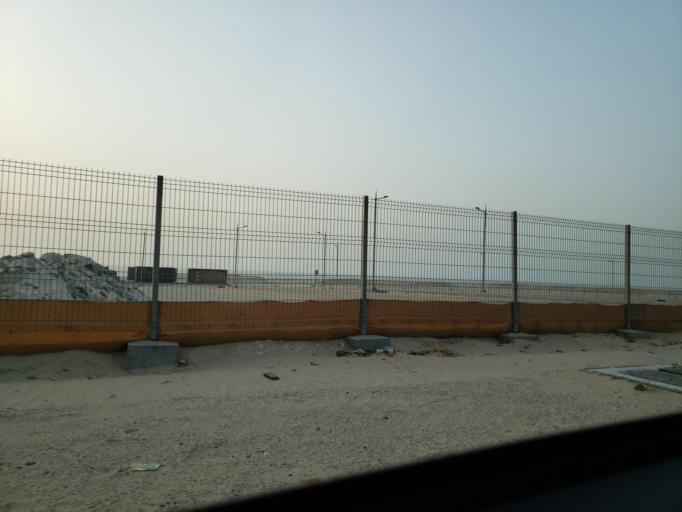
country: AE
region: Ajman
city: Ajman
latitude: 25.4311
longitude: 55.4593
